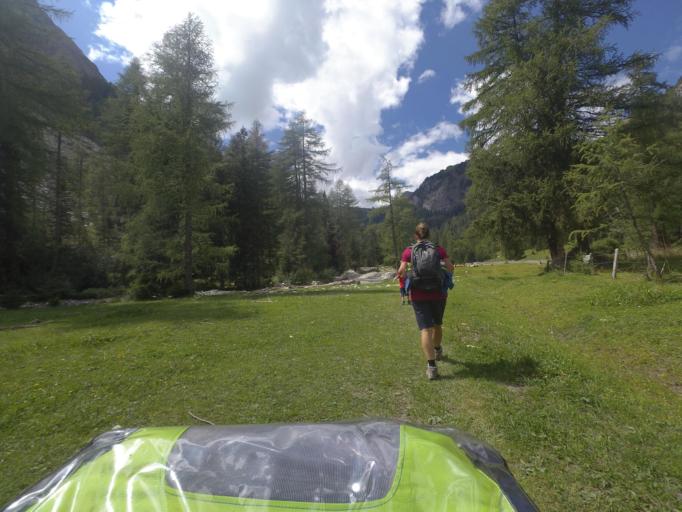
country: AT
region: Salzburg
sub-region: Politischer Bezirk Sankt Johann im Pongau
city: Kleinarl
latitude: 47.1871
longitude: 13.3783
